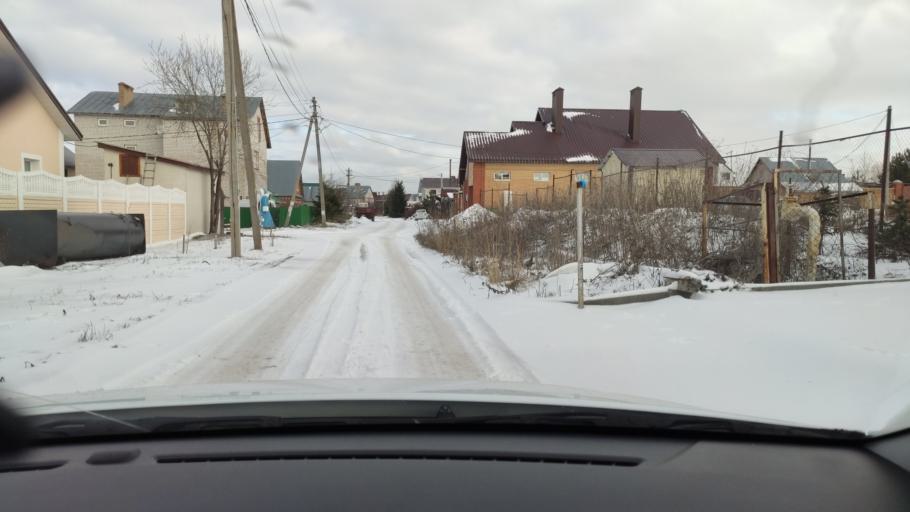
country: RU
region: Tatarstan
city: Stolbishchi
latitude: 55.7701
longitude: 49.2703
